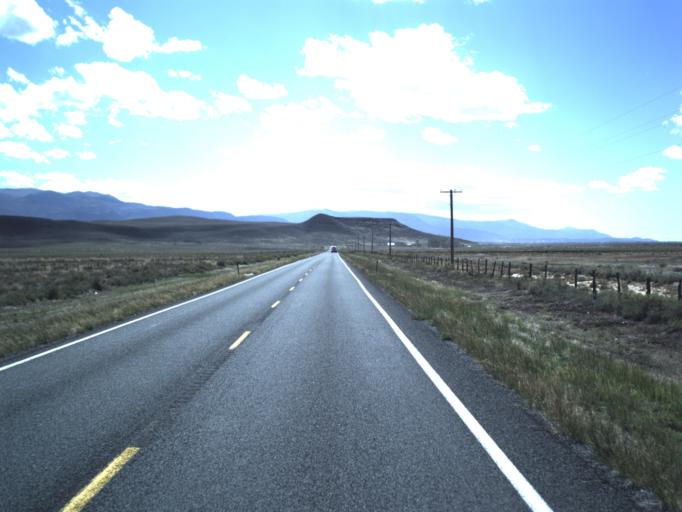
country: US
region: Utah
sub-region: Iron County
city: Enoch
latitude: 37.8716
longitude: -113.0317
